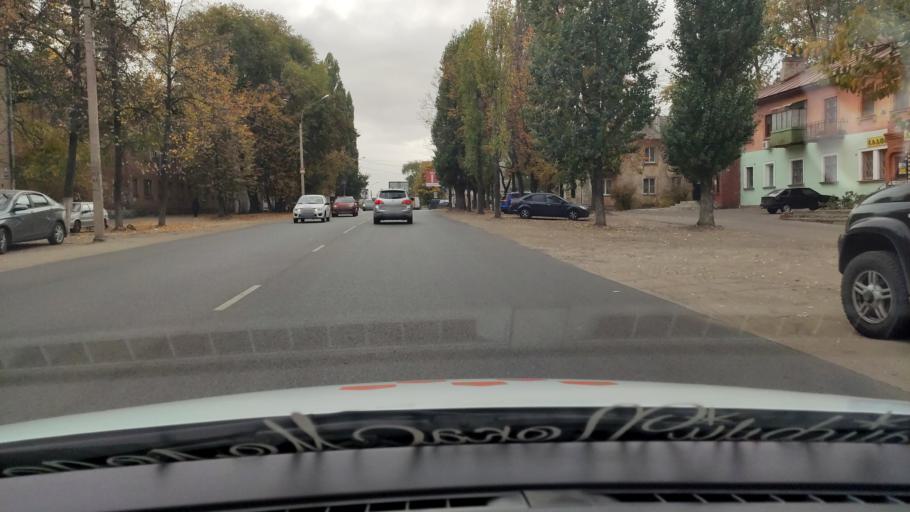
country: RU
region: Voronezj
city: Voronezh
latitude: 51.6766
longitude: 39.1576
